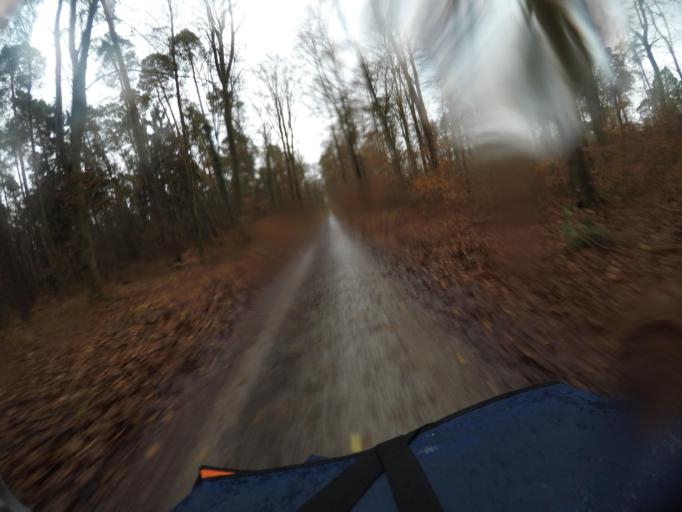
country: DE
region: Baden-Wuerttemberg
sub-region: Karlsruhe Region
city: Linkenheim-Hochstetten
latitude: 49.1246
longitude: 8.4507
